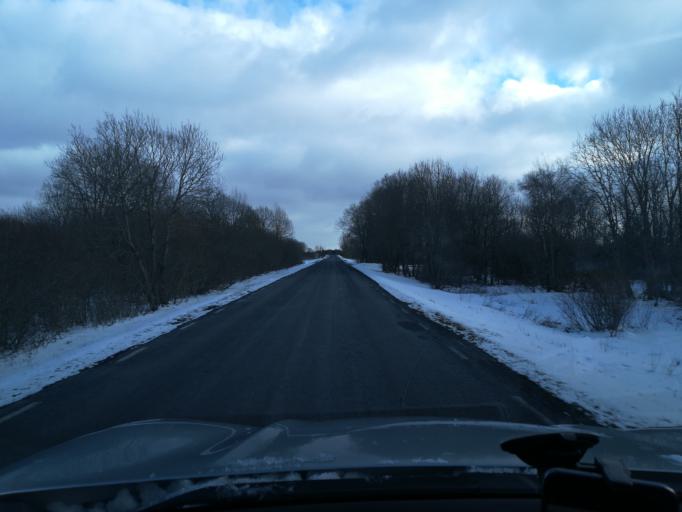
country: EE
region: Harju
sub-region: Keila linn
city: Keila
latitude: 59.4358
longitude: 24.3999
